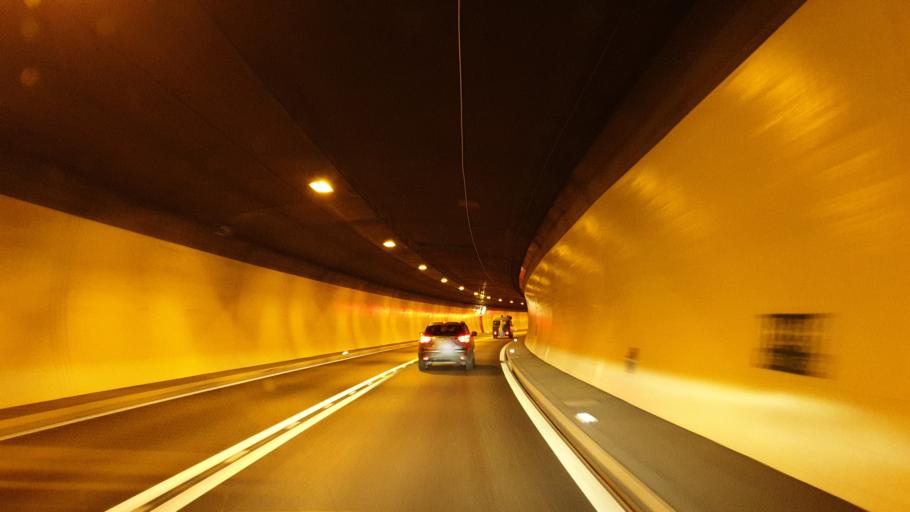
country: CH
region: Uri
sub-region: Uri
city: Flueelen
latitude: 46.9142
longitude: 8.6257
